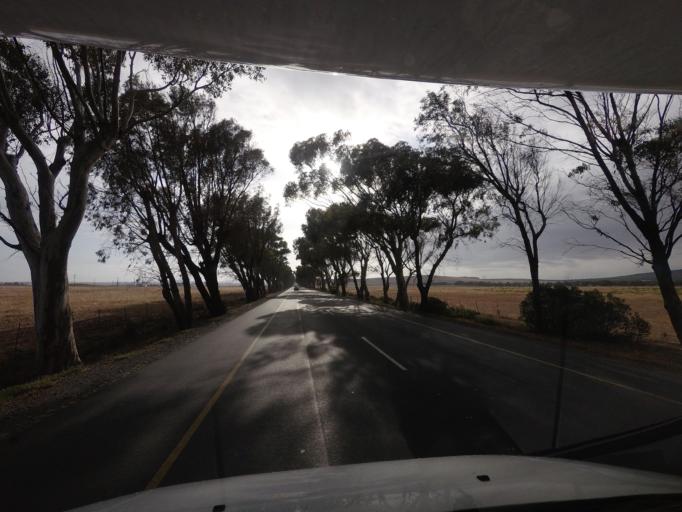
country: ZA
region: Western Cape
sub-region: City of Cape Town
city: Sunset Beach
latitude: -33.7255
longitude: 18.4626
